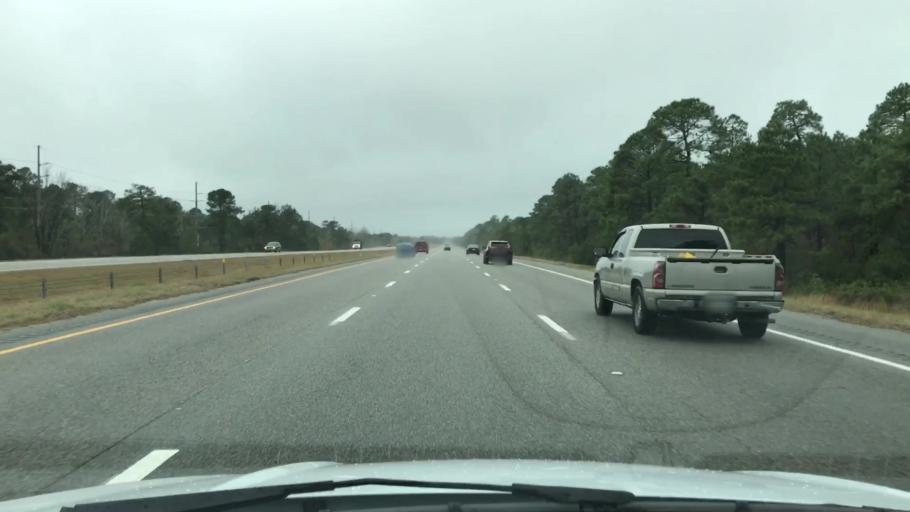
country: US
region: South Carolina
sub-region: Horry County
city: Forestbrook
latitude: 33.7478
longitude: -78.9101
